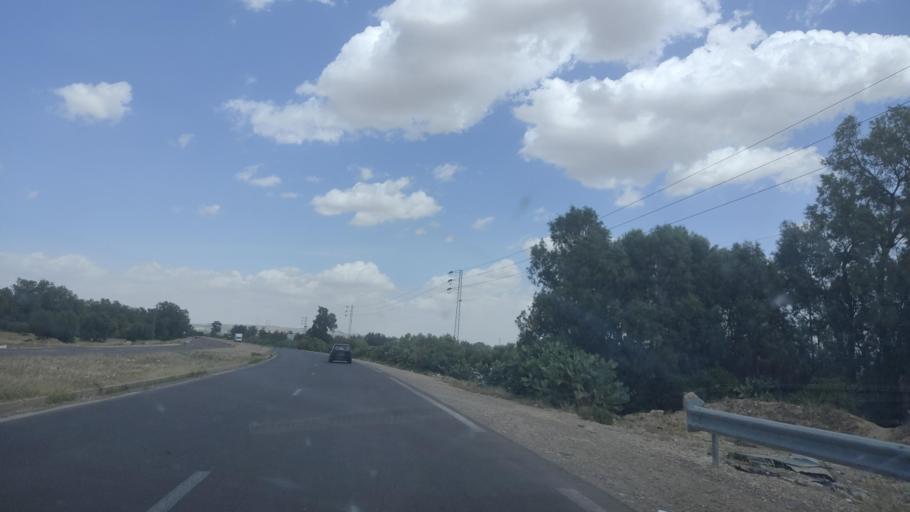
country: TN
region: Al Qasrayn
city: Kasserine
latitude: 35.1973
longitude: 8.8688
